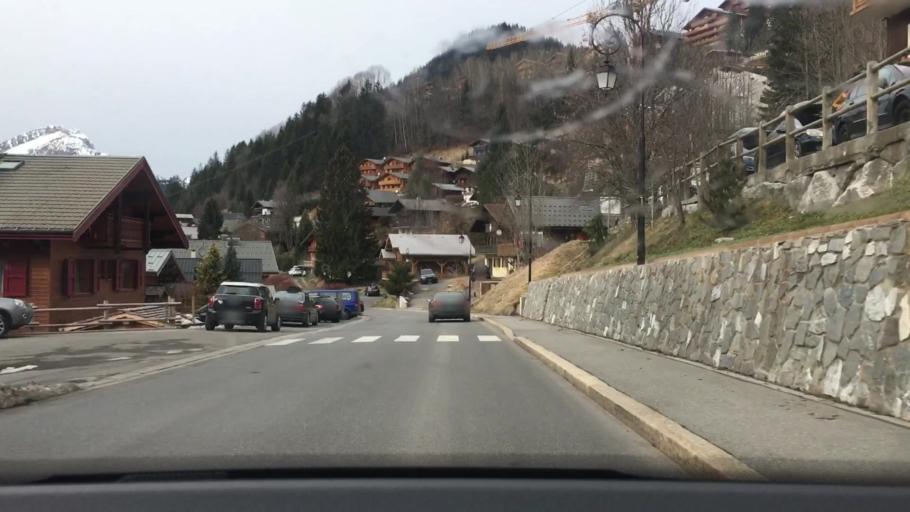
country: FR
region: Rhone-Alpes
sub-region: Departement de la Haute-Savoie
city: Chatel
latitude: 46.2743
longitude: 6.8367
